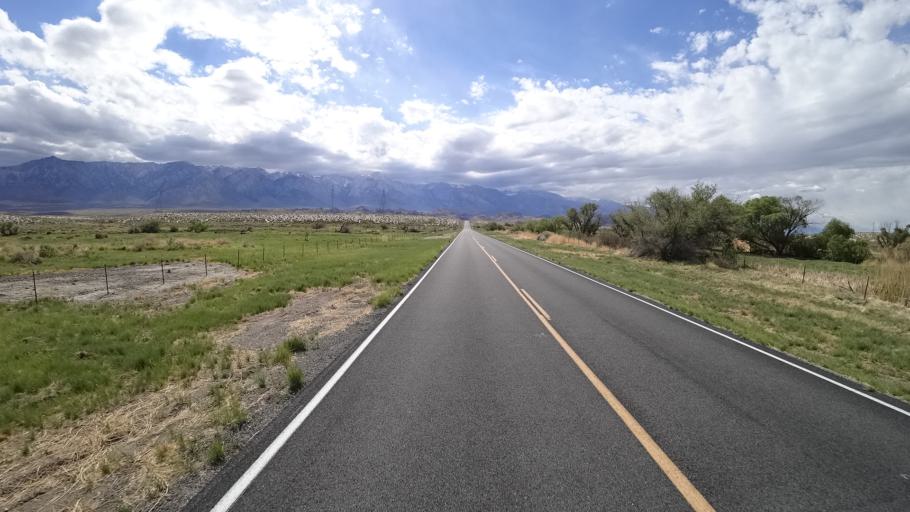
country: US
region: California
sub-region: Inyo County
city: Lone Pine
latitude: 36.5746
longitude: -118.0119
